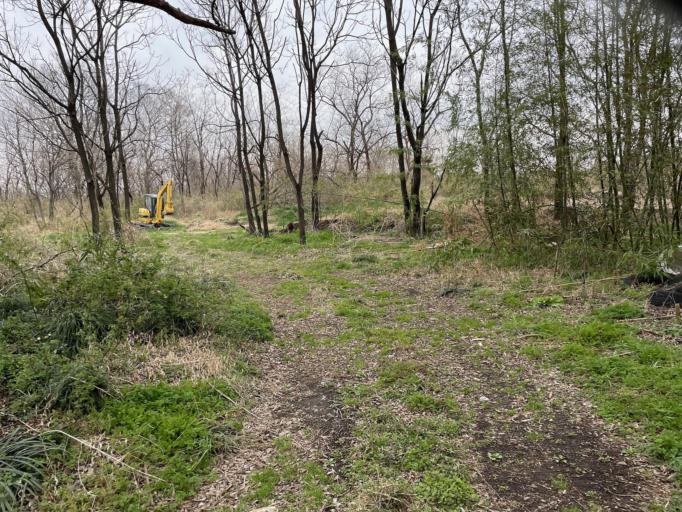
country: JP
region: Gunma
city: Fujioka
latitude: 36.2320
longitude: 139.0961
